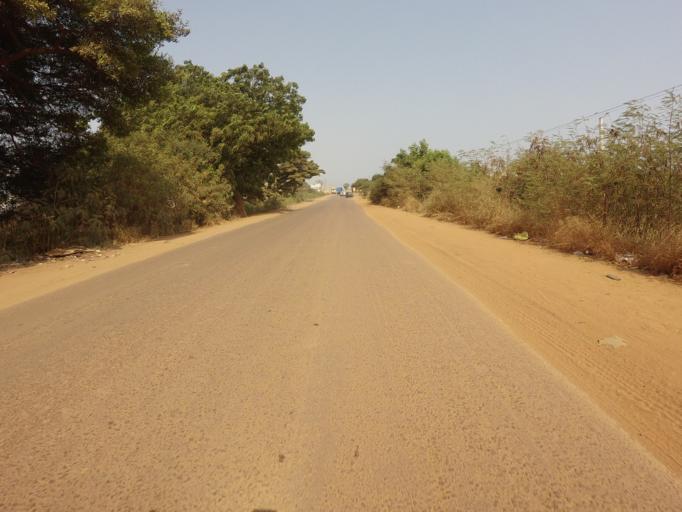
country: GH
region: Greater Accra
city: Tema
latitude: 5.6686
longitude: 0.0139
